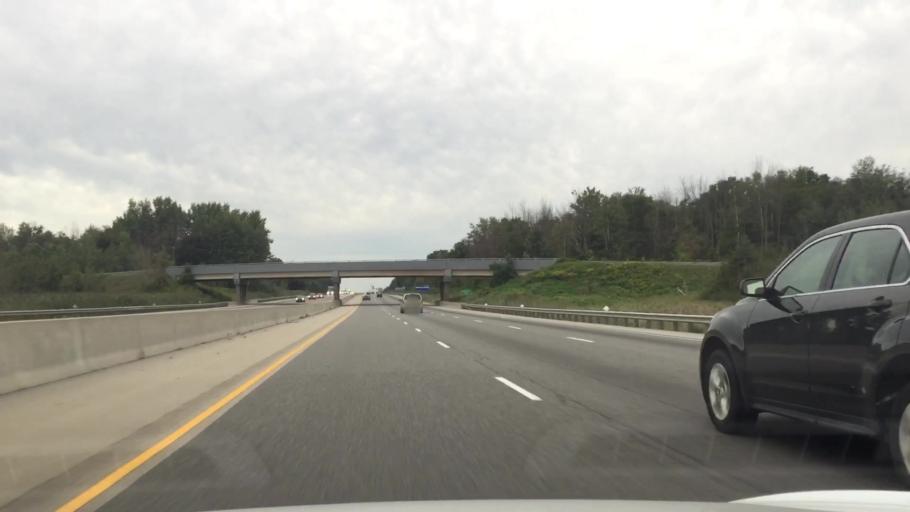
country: CA
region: Ontario
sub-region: Oxford County
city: Woodstock
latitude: 43.1670
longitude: -80.6629
